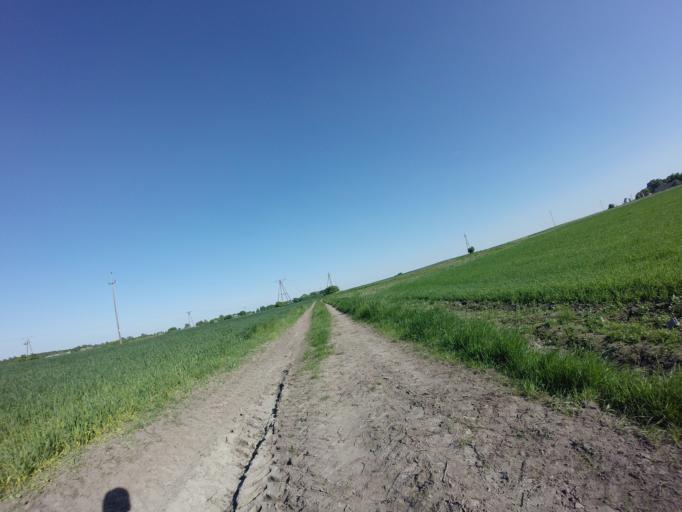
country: PL
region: West Pomeranian Voivodeship
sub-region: Powiat choszczenski
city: Choszczno
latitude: 53.1508
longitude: 15.4103
